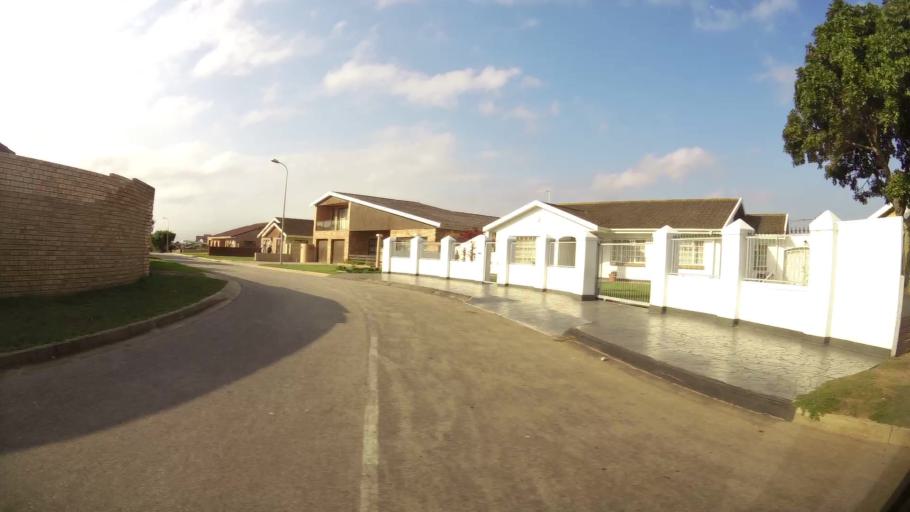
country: ZA
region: Eastern Cape
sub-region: Nelson Mandela Bay Metropolitan Municipality
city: Port Elizabeth
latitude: -33.9218
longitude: 25.5619
